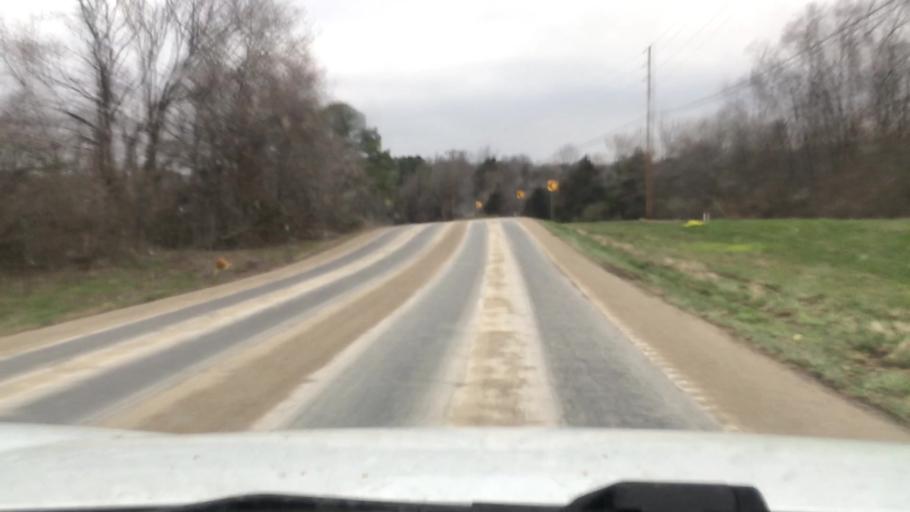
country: US
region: Missouri
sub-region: Saint Charles County
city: Weldon Spring
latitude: 38.6702
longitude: -90.7317
